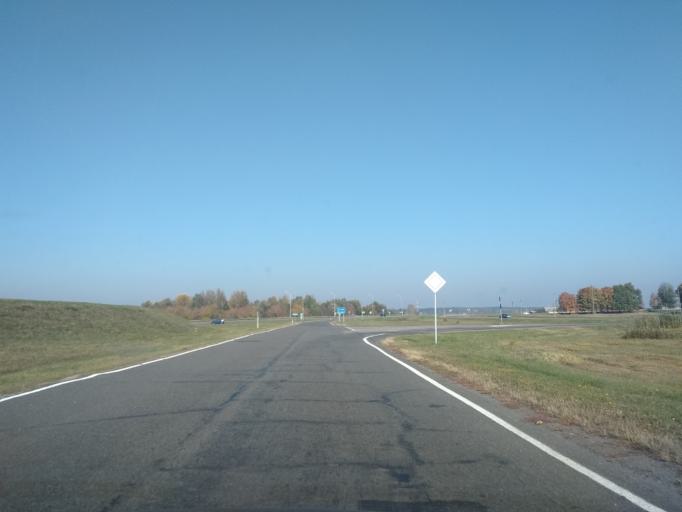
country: BY
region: Brest
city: Ivatsevichy
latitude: 52.6982
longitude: 25.3649
